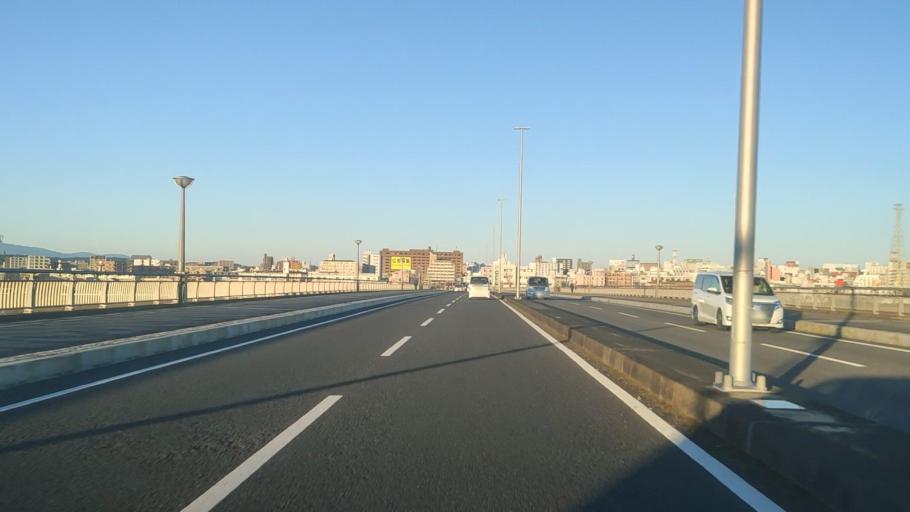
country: JP
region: Miyazaki
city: Miyazaki-shi
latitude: 31.9078
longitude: 131.4110
